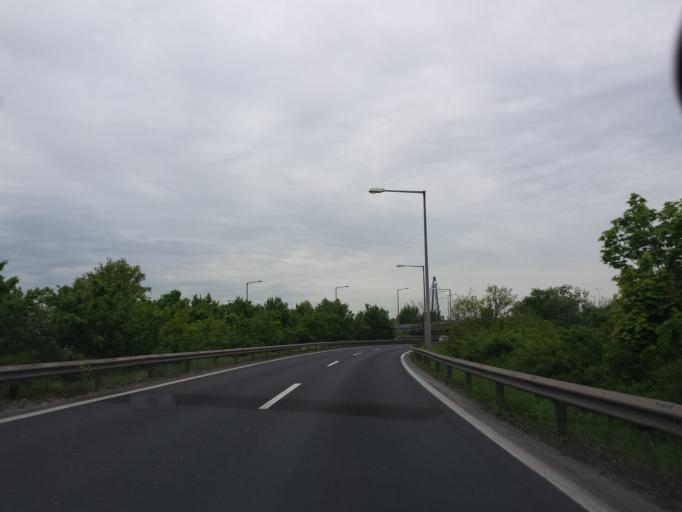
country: AT
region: Vienna
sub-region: Wien Stadt
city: Vienna
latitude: 48.2109
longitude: 16.4447
